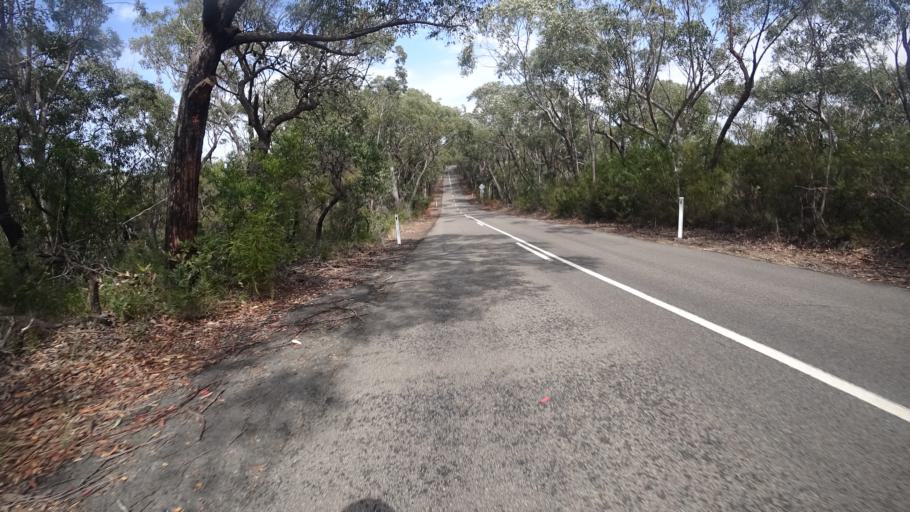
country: AU
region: New South Wales
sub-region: Hornsby Shire
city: Mount Colah
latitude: -33.6755
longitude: 151.1324
